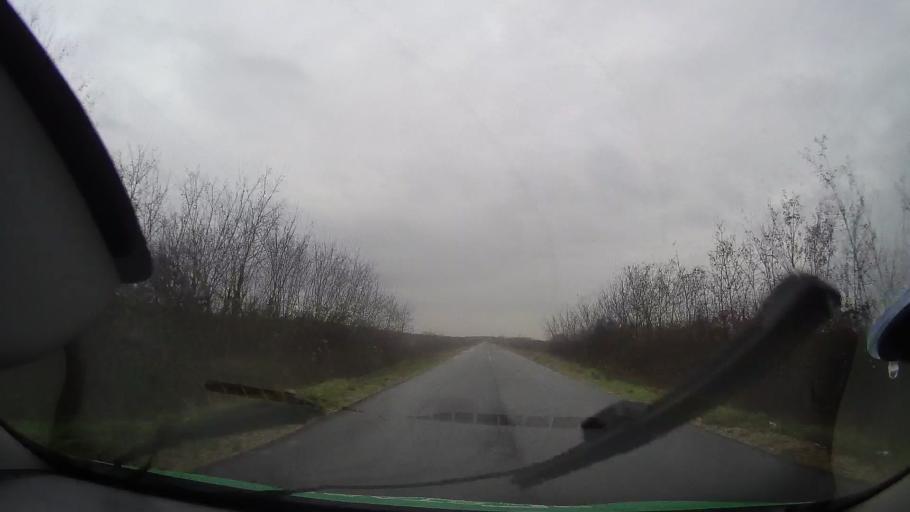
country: RO
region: Bihor
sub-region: Comuna Olcea
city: Olcea
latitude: 46.6953
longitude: 22.0290
